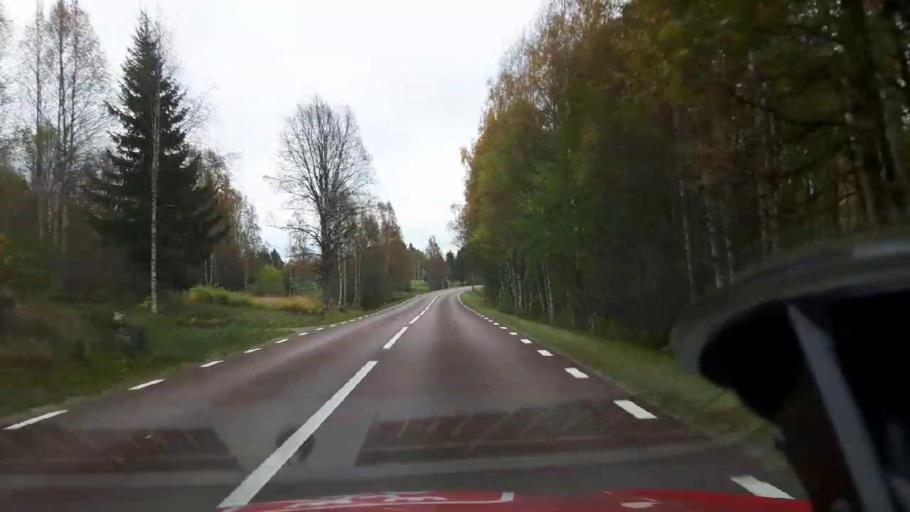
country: SE
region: Jaemtland
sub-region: Harjedalens Kommun
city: Sveg
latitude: 62.3097
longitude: 14.7609
